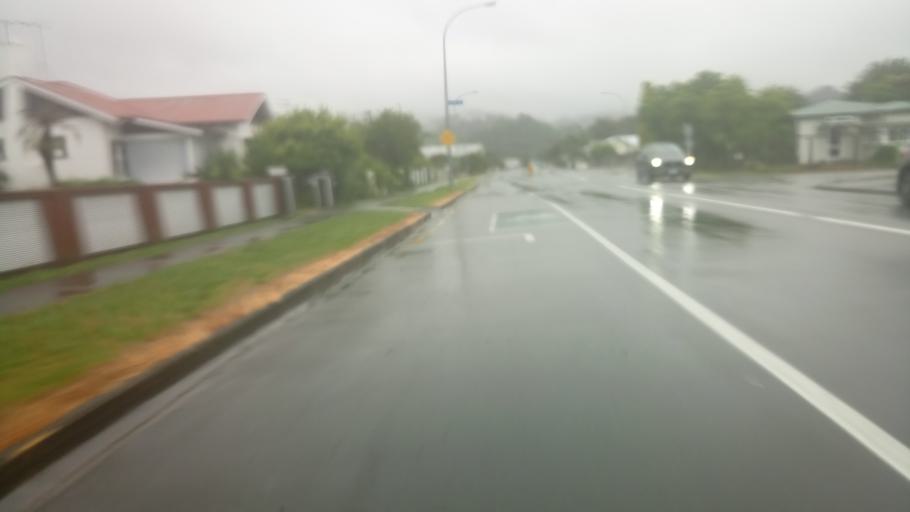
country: NZ
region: Gisborne
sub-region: Gisborne District
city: Gisborne
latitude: -38.6581
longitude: 178.0158
